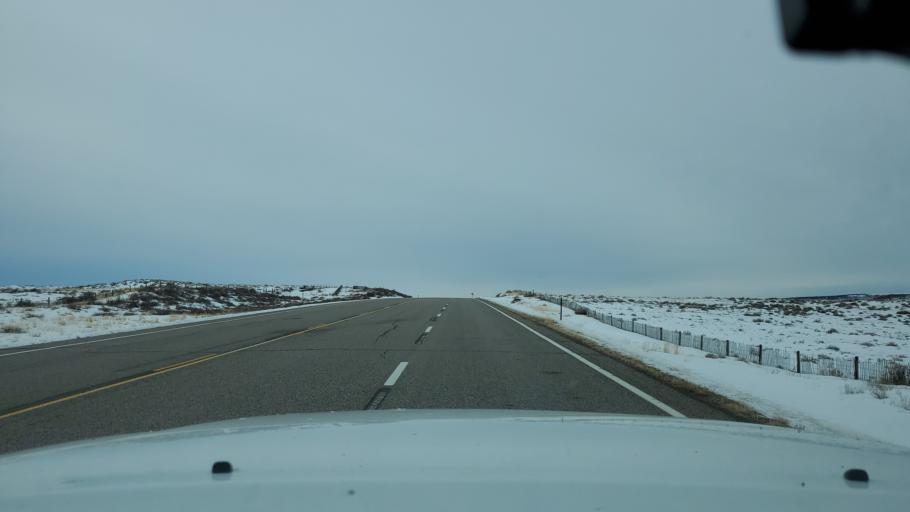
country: US
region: Colorado
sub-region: Rio Blanco County
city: Meeker
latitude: 40.4813
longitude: -108.1900
